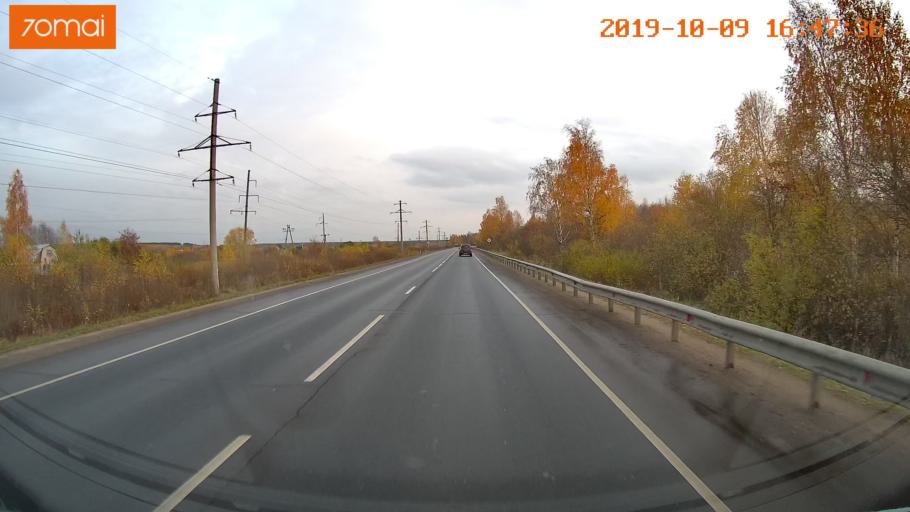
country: RU
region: Kostroma
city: Volgorechensk
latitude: 57.4357
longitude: 41.1801
